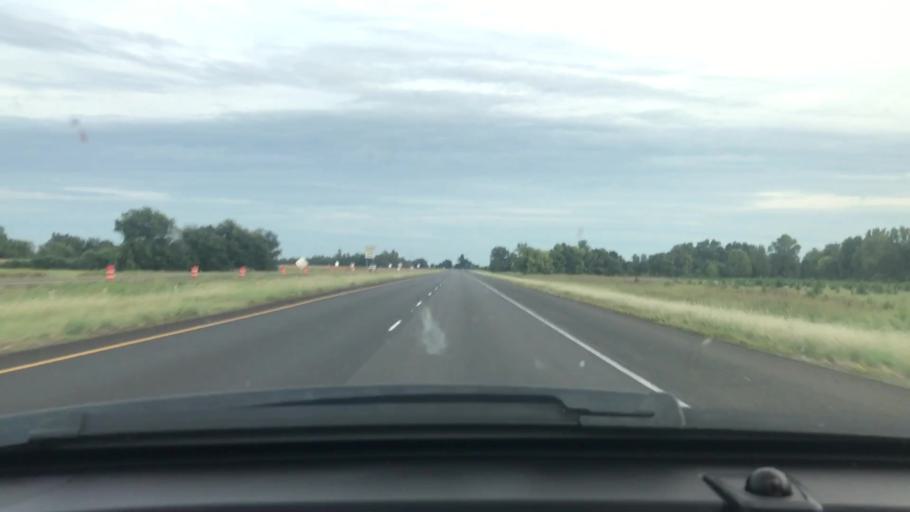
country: US
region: Arkansas
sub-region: Poinsett County
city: Trumann
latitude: 35.6690
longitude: -90.5525
